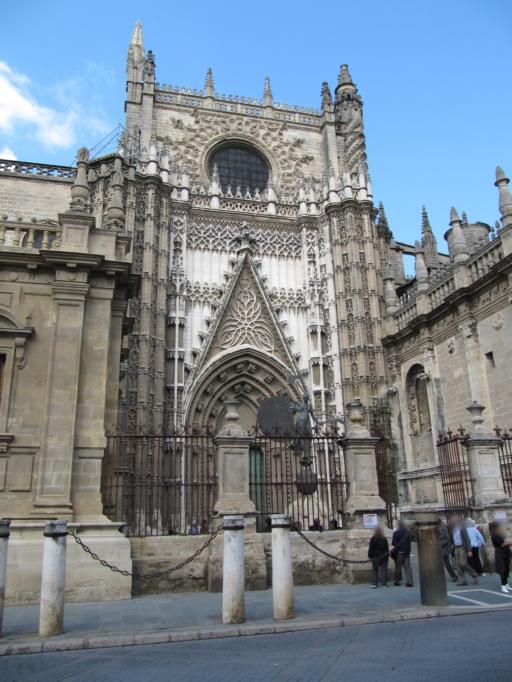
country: ES
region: Andalusia
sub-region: Provincia de Sevilla
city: Sevilla
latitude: 37.3851
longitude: -5.9931
